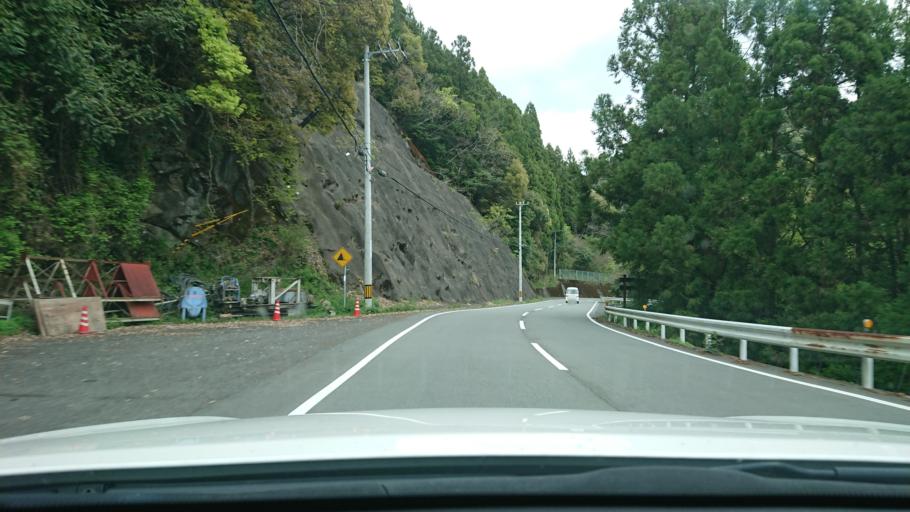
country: JP
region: Tokushima
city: Ishii
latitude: 33.9087
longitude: 134.4204
